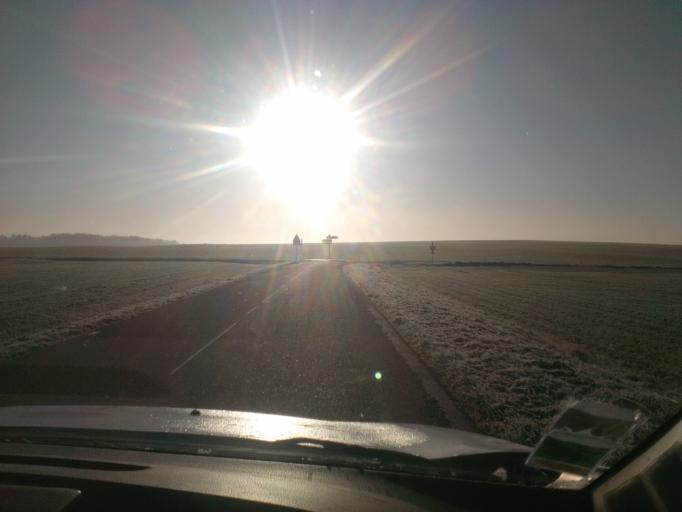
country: FR
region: Lorraine
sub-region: Departement des Vosges
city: Darnieulles
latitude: 48.1929
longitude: 6.2298
